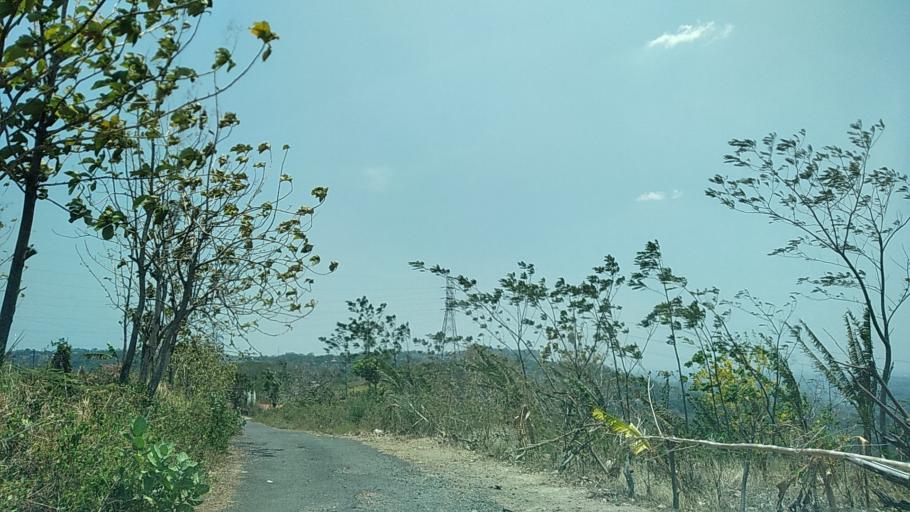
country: ID
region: Central Java
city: Ungaran
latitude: -7.0869
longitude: 110.4371
